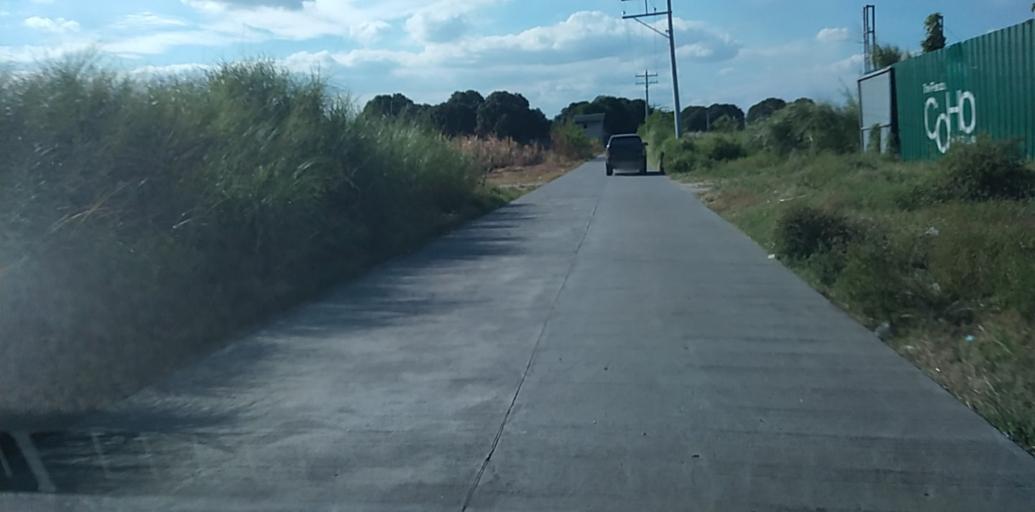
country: PH
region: Central Luzon
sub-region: Province of Pampanga
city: Acli
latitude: 15.1102
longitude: 120.6516
